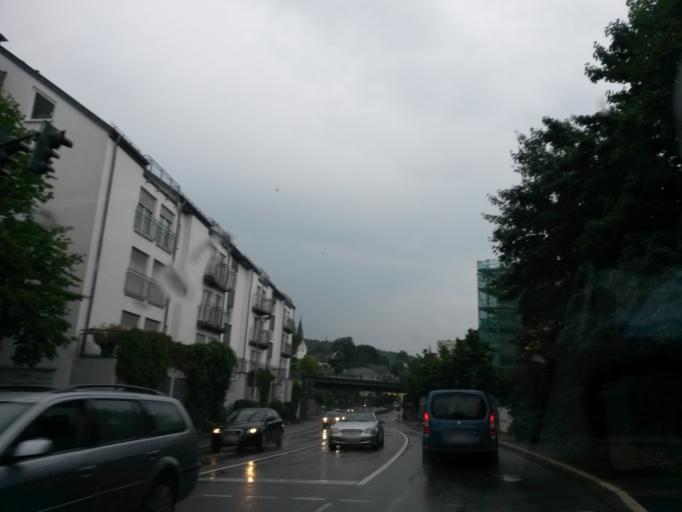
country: DE
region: North Rhine-Westphalia
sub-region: Regierungsbezirk Koln
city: Gummersbach
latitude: 51.0258
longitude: 7.5615
